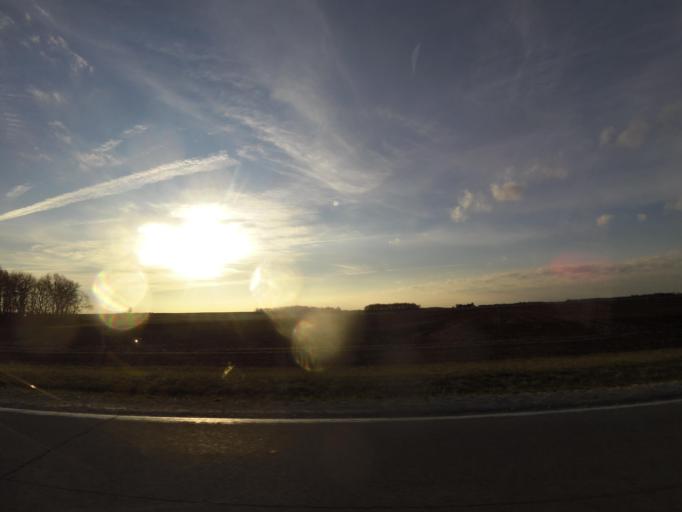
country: US
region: Illinois
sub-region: Fayette County
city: Vandalia
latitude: 38.9504
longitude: -89.1400
